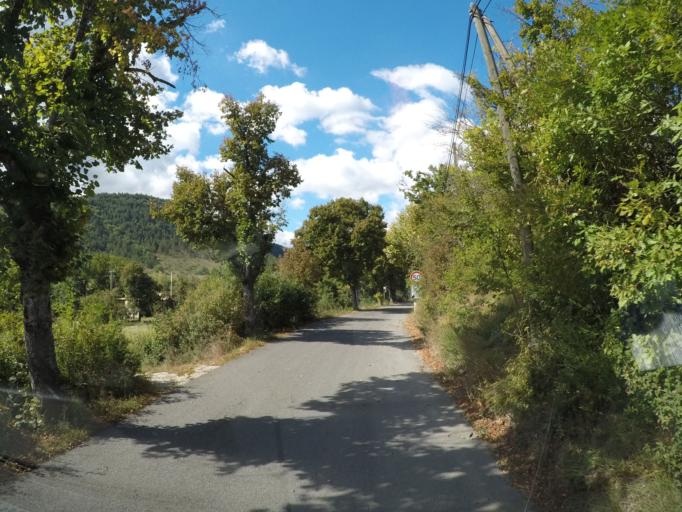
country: FR
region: Provence-Alpes-Cote d'Azur
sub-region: Departement des Hautes-Alpes
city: Laragne-Monteglin
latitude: 44.1716
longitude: 5.7399
